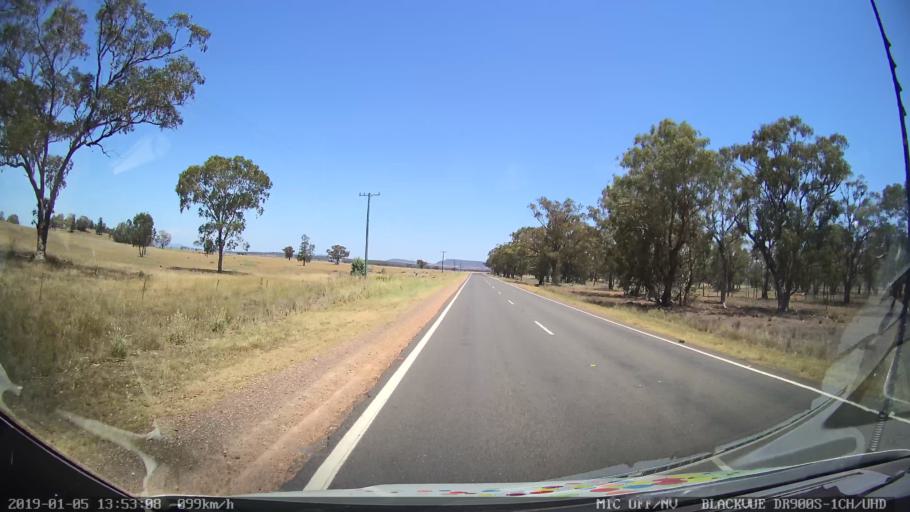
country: AU
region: New South Wales
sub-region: Gunnedah
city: Gunnedah
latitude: -31.0704
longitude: 150.2770
